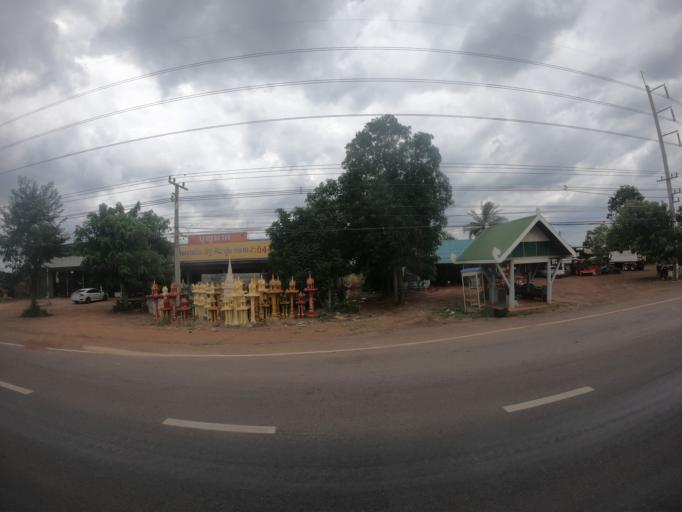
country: TH
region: Nakhon Ratchasima
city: Nong Bun Nak
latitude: 14.7411
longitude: 102.3685
